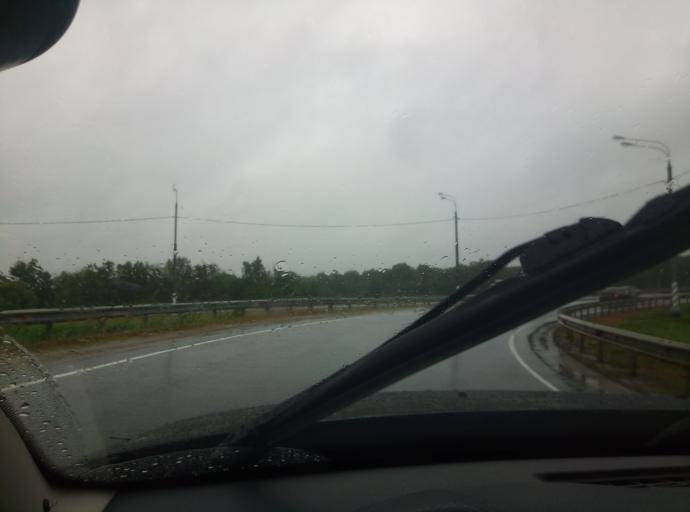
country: RU
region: Tula
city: Leninskiy
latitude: 54.4109
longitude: 37.4963
